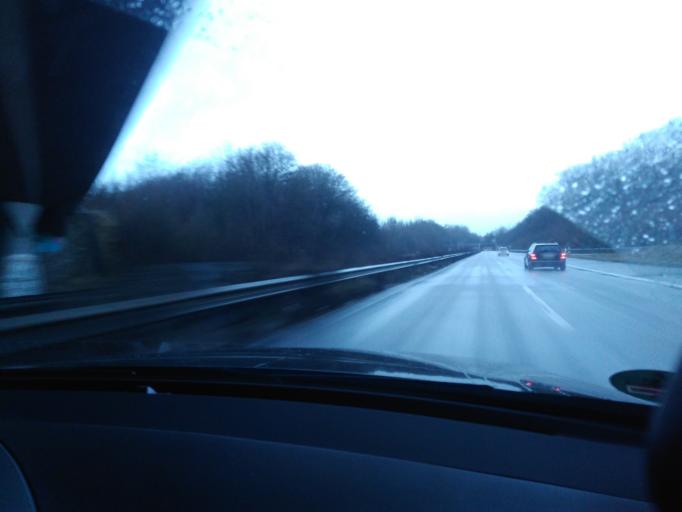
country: DE
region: Schleswig-Holstein
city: Kiel
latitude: 54.3495
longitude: 10.1203
